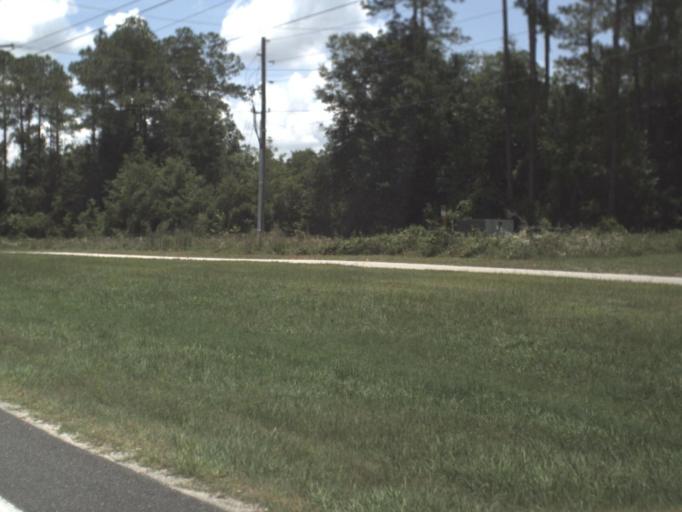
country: US
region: Florida
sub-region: Alachua County
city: Archer
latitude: 29.5902
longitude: -82.4378
